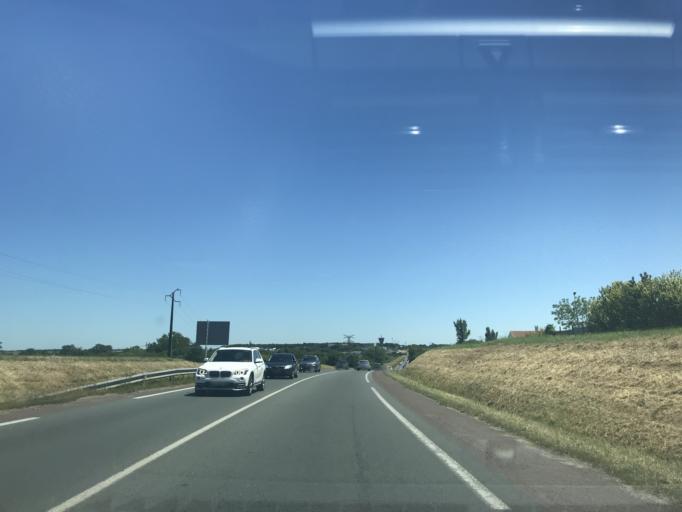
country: FR
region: Poitou-Charentes
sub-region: Departement de la Charente-Maritime
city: Royan
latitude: 45.6382
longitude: -1.0206
